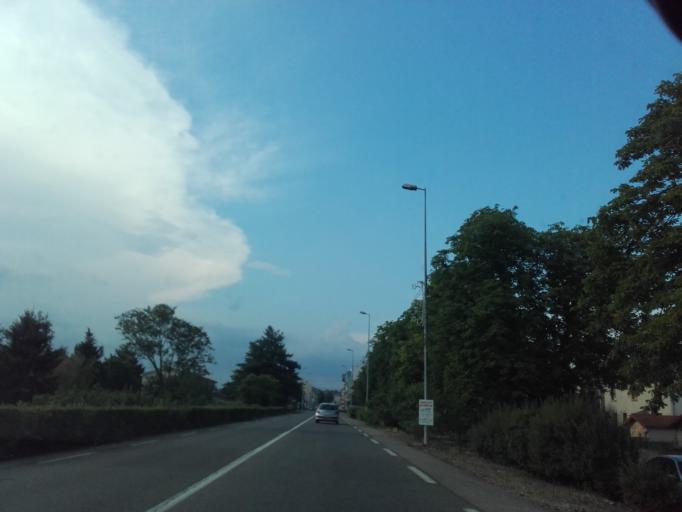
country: FR
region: Rhone-Alpes
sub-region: Departement de l'Isere
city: Le Peage-de-Roussillon
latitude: 45.3593
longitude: 4.8013
